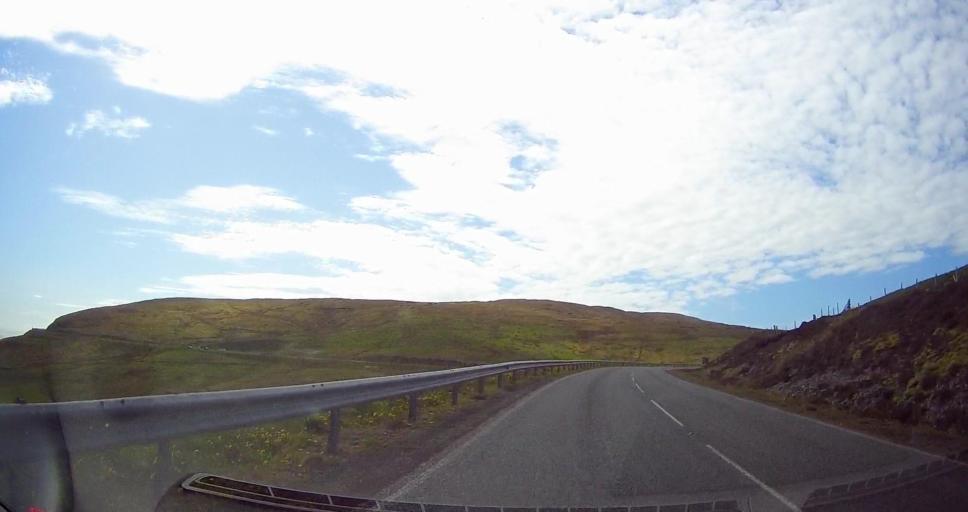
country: GB
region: Scotland
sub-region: Shetland Islands
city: Sandwick
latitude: 59.9899
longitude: -1.2841
